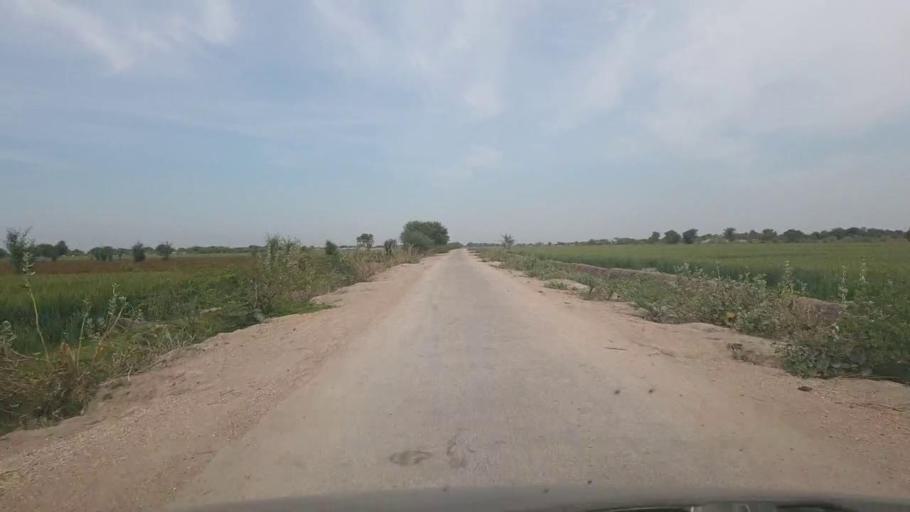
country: PK
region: Sindh
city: Kunri
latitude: 25.2484
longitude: 69.6218
